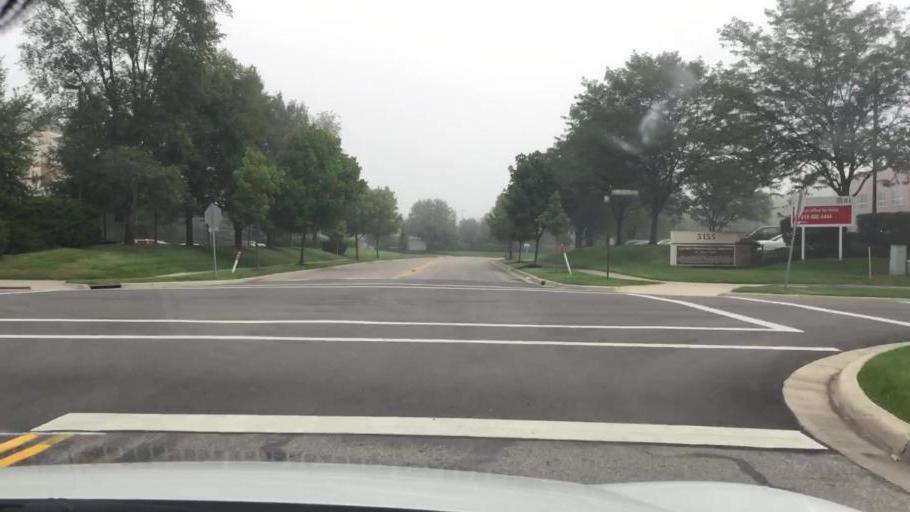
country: US
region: Ohio
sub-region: Franklin County
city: Dublin
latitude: 40.0794
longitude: -83.1281
